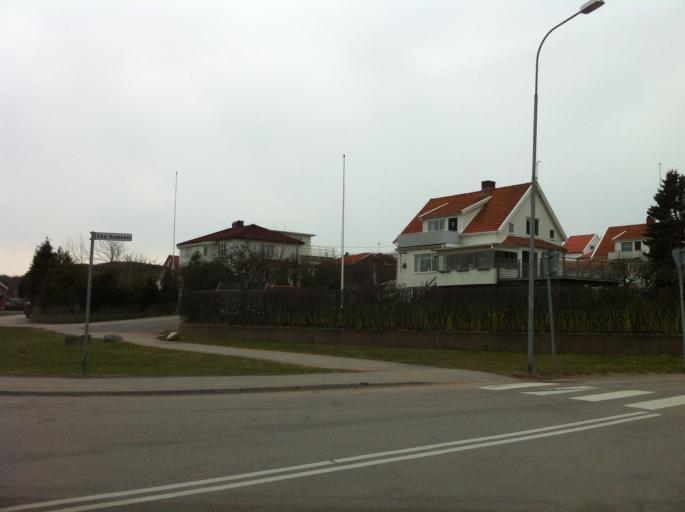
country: SE
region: Vaestra Goetaland
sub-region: Orust
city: Henan
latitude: 58.1569
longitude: 11.7057
